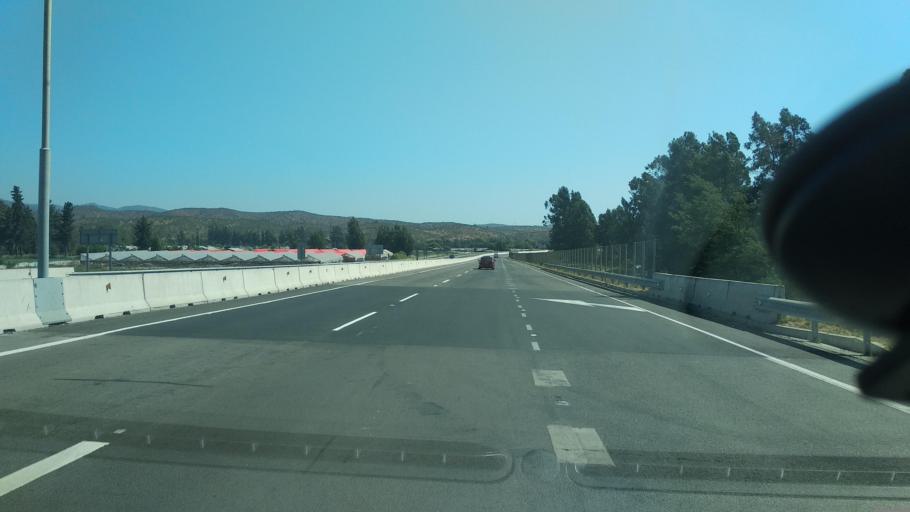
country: CL
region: Valparaiso
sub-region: Provincia de Marga Marga
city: Limache
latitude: -32.9749
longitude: -71.3035
